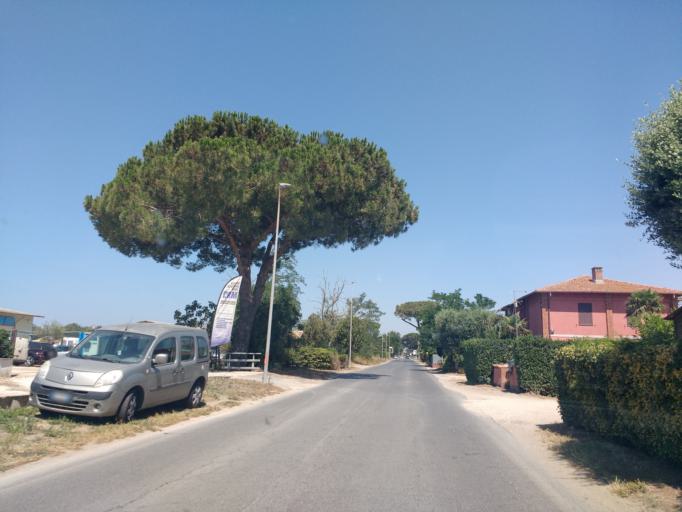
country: IT
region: Latium
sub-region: Citta metropolitana di Roma Capitale
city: Fregene
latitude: 41.8447
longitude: 12.2228
